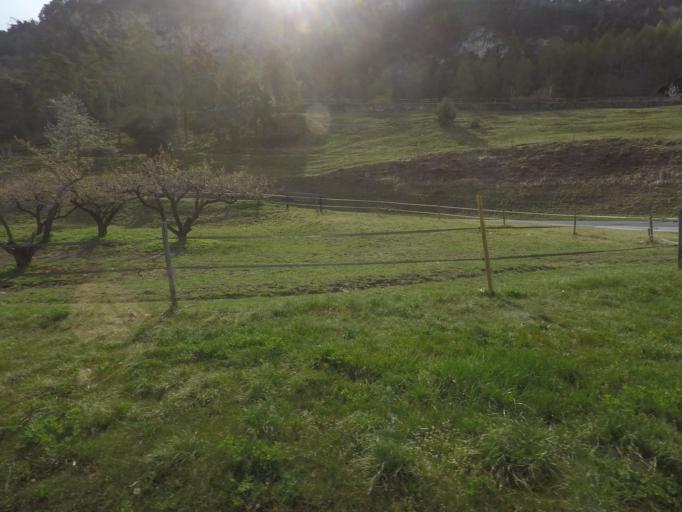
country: CH
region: Valais
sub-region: Herens District
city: Vex
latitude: 46.2218
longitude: 7.3867
